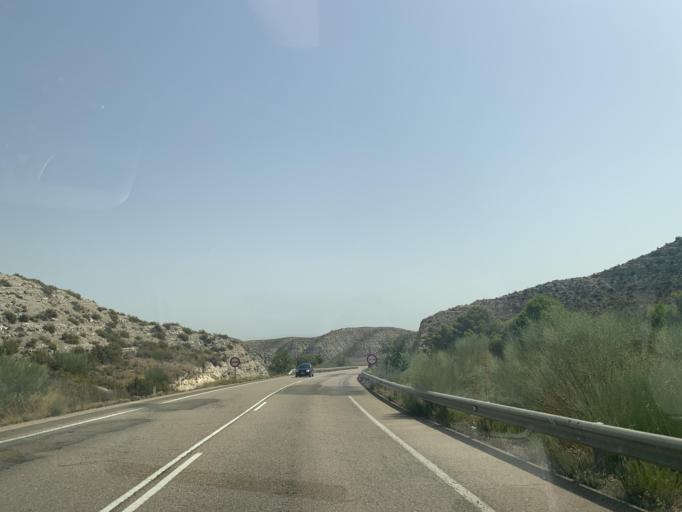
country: ES
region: Aragon
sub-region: Provincia de Zaragoza
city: El Burgo de Ebro
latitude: 41.5264
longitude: -0.7020
